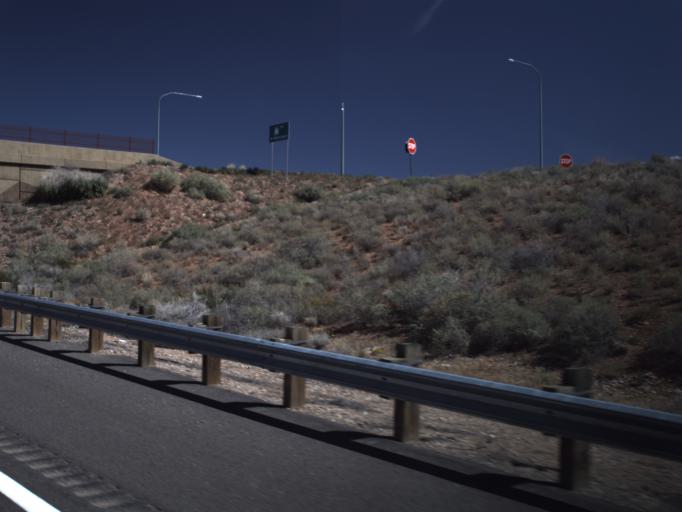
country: US
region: Utah
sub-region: Washington County
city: Washington
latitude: 37.0142
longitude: -113.4950
